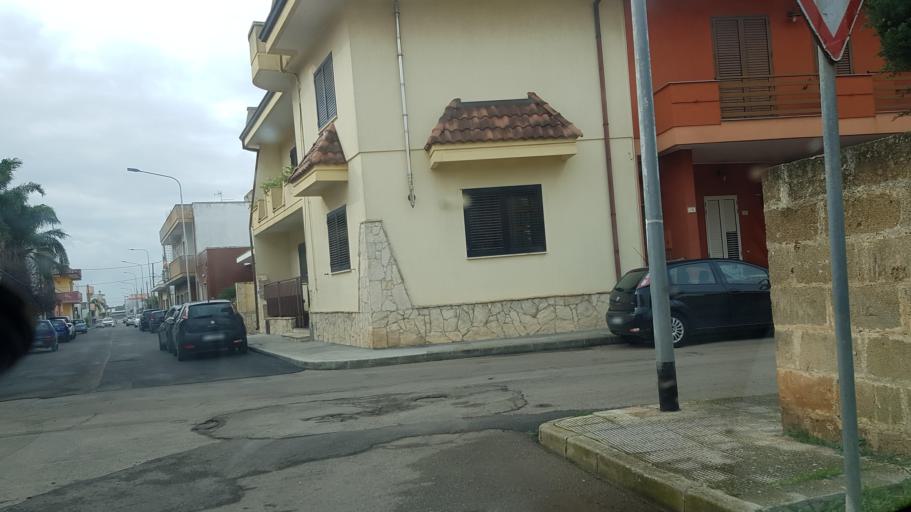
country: IT
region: Apulia
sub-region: Provincia di Lecce
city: Carmiano
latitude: 40.3413
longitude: 18.0478
